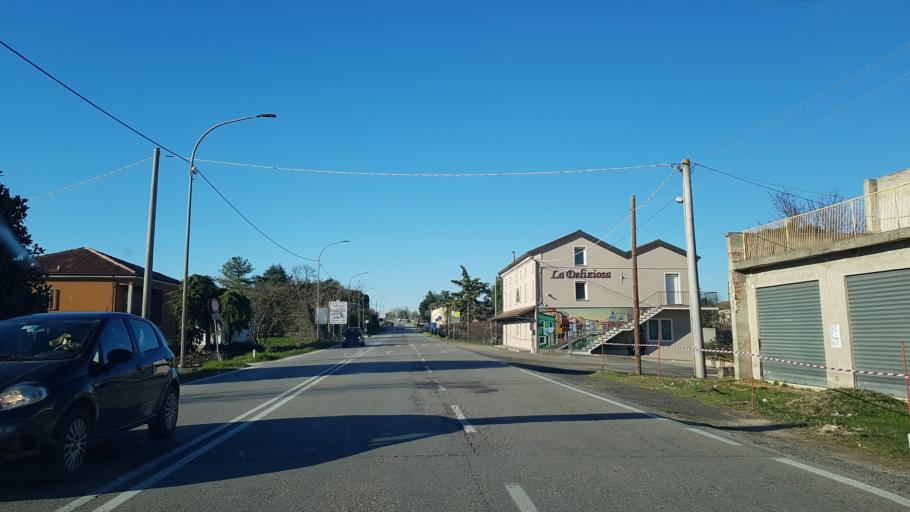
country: IT
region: Veneto
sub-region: Provincia di Padova
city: Boara Pisani
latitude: 45.1003
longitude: 11.7856
